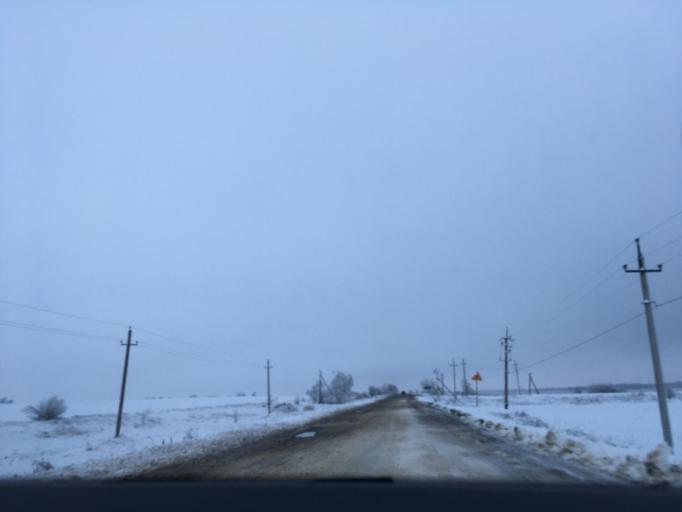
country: RU
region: Voronezj
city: Verkhniy Mamon
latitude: 50.0290
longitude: 40.0707
